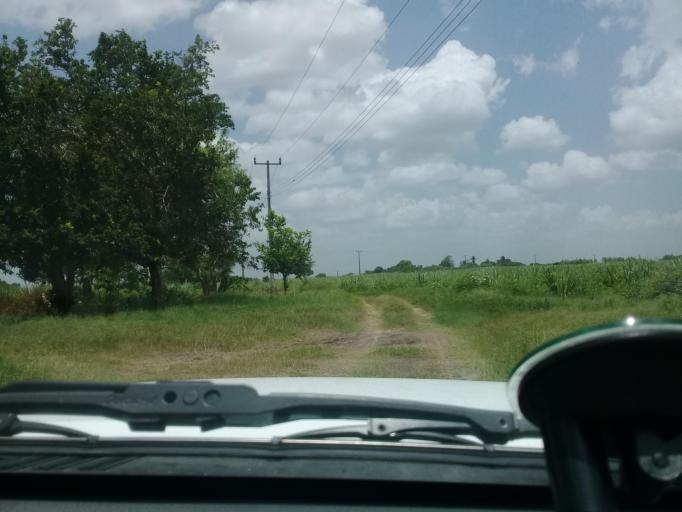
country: MX
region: Veracruz
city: Moralillo
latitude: 22.1322
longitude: -98.0357
